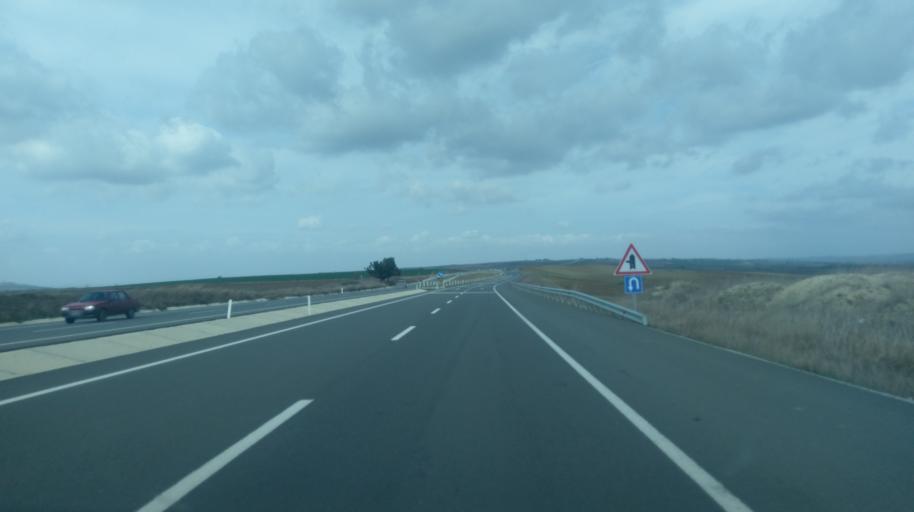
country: TR
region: Edirne
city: Hamidiye
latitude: 41.0231
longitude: 26.6352
